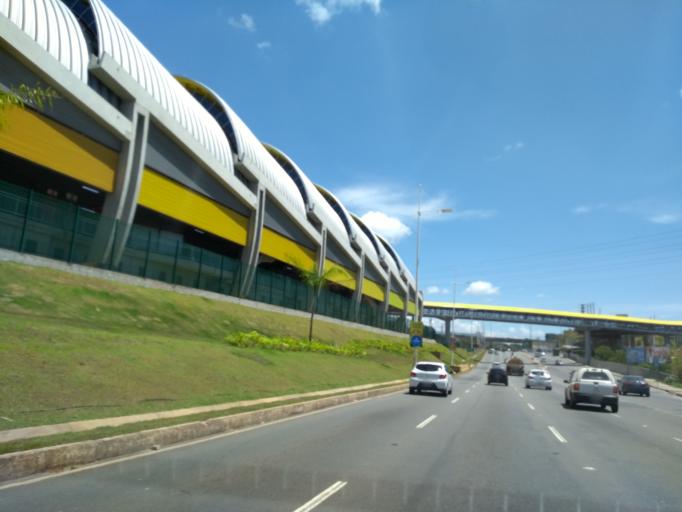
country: BR
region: Bahia
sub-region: Salvador
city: Salvador
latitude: -12.9458
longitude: -38.4213
